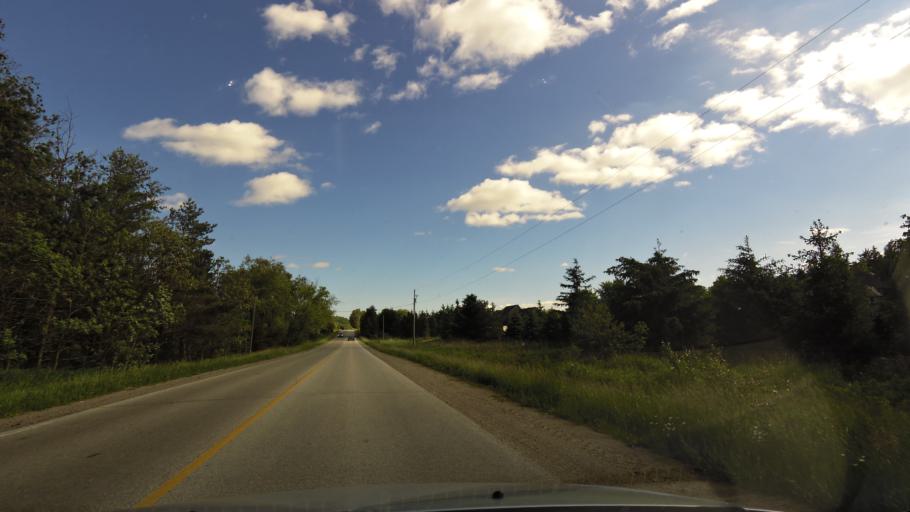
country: CA
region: Ontario
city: Bradford West Gwillimbury
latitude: 44.1839
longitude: -79.6211
